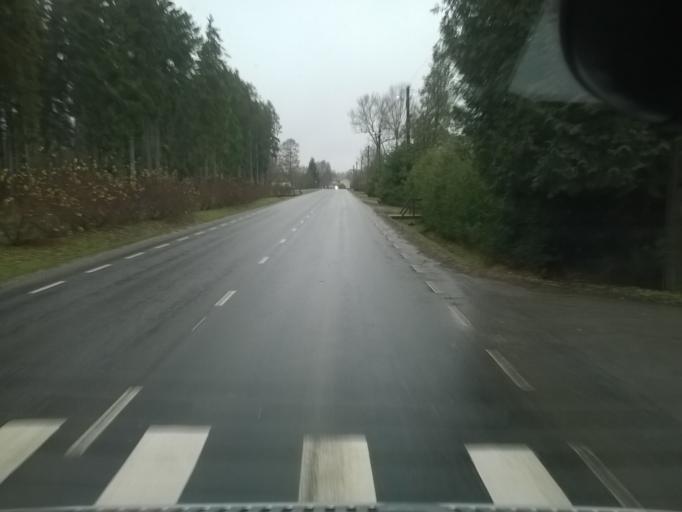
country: EE
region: Harju
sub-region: Saku vald
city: Saku
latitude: 59.2366
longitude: 24.6825
